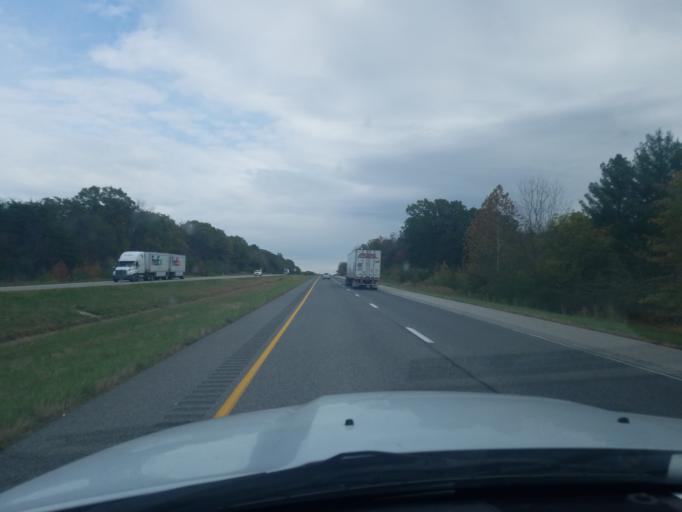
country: US
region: Indiana
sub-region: Warrick County
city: Boonville
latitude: 38.2008
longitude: -87.2226
